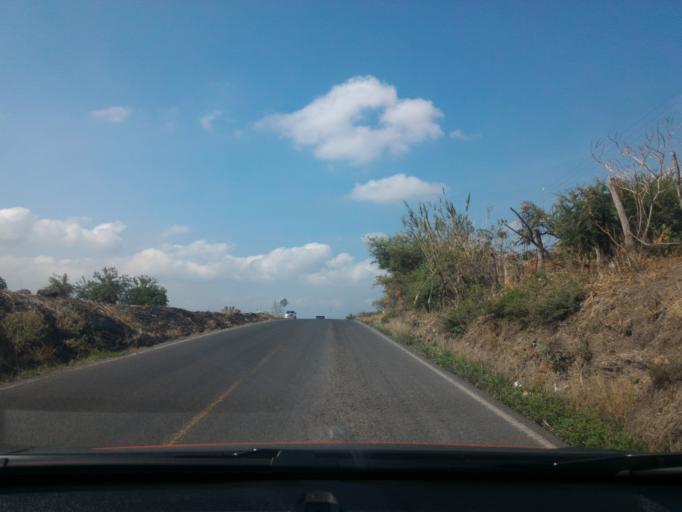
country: MX
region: Guanajuato
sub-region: Penjamo
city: Estacion la Piedad
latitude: 20.4311
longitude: -101.9902
